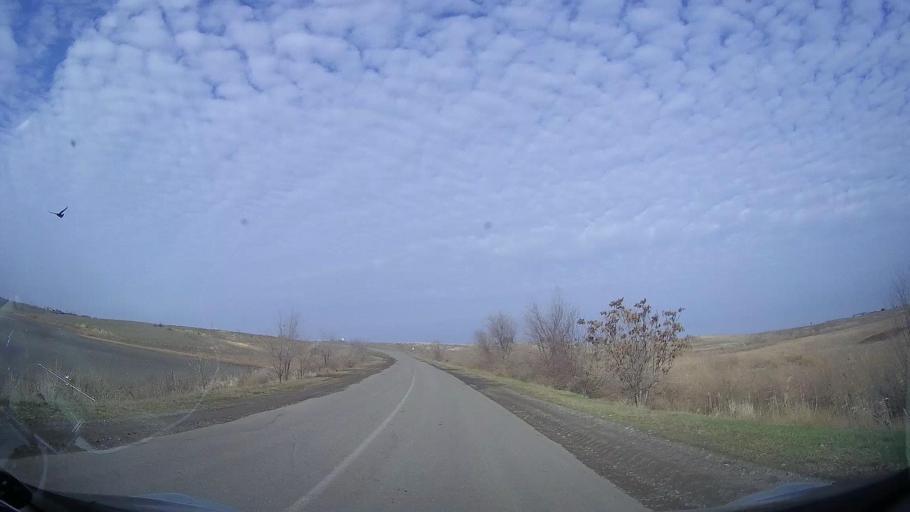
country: RU
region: Rostov
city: Gigant
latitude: 46.8427
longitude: 41.3310
